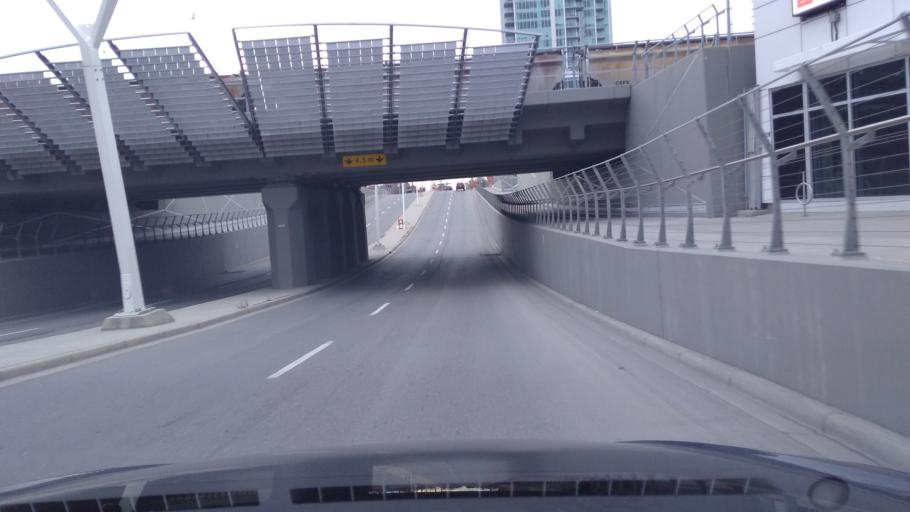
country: CA
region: Alberta
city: Calgary
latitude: 51.0440
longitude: -114.0534
